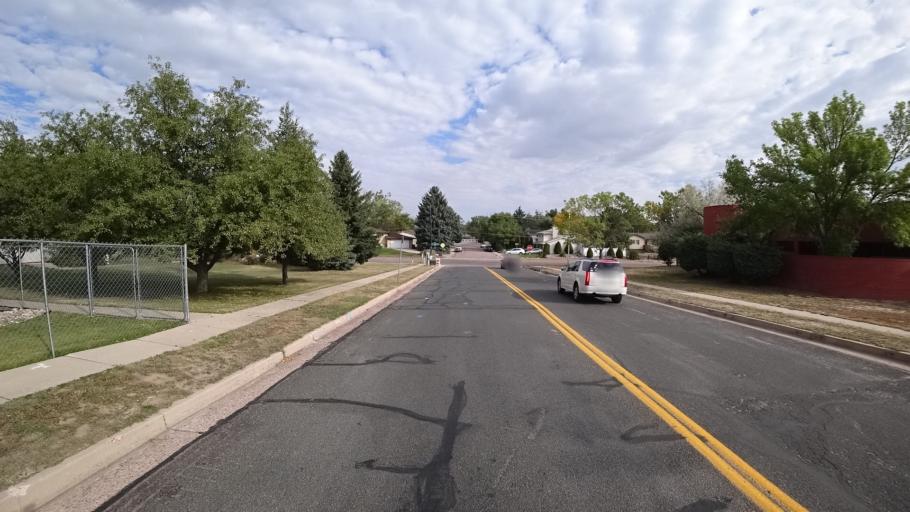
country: US
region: Colorado
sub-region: El Paso County
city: Cimarron Hills
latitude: 38.8466
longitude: -104.7458
